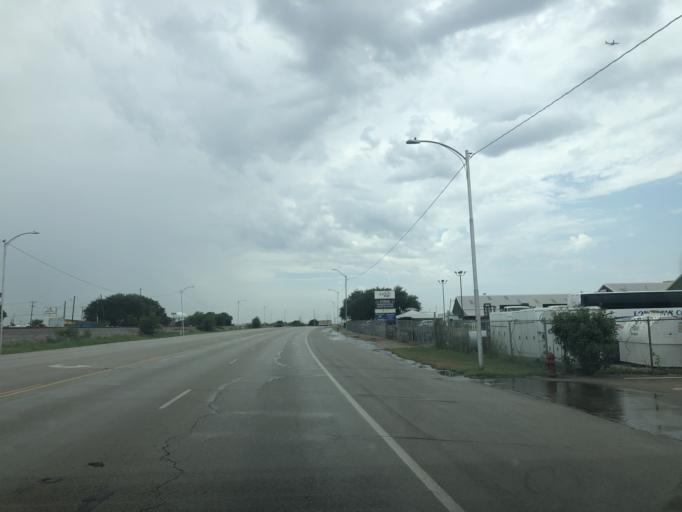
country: US
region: Texas
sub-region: Dallas County
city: Grand Prairie
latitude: 32.7394
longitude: -97.0395
